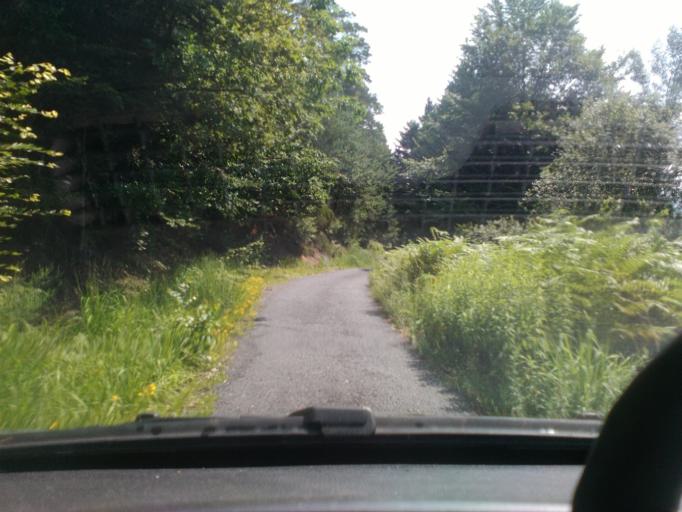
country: FR
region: Lorraine
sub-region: Departement des Vosges
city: Sainte-Marguerite
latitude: 48.2992
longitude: 6.9917
